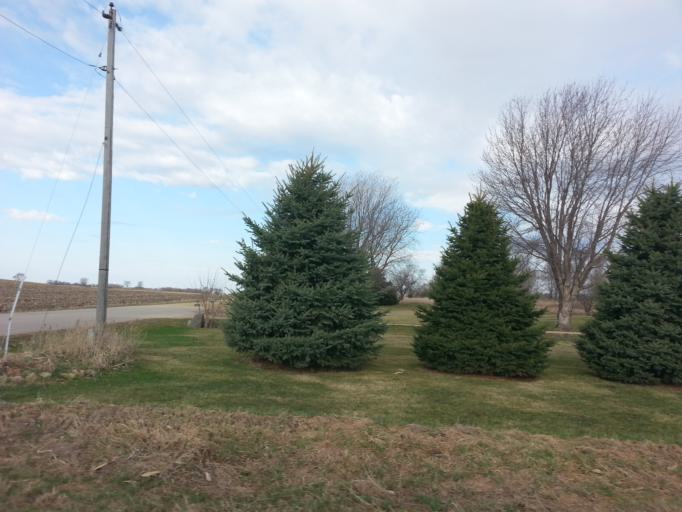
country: US
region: Minnesota
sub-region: Dakota County
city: Hastings
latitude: 44.8046
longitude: -92.8421
